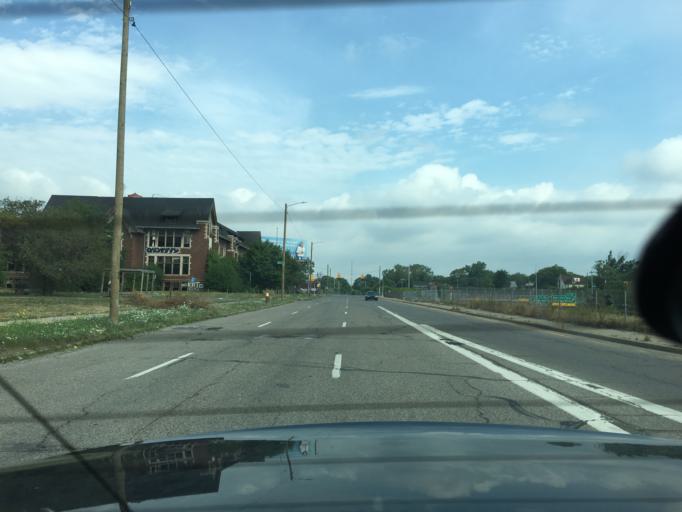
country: US
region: Michigan
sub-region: Wayne County
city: Highland Park
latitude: 42.3782
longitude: -83.0899
